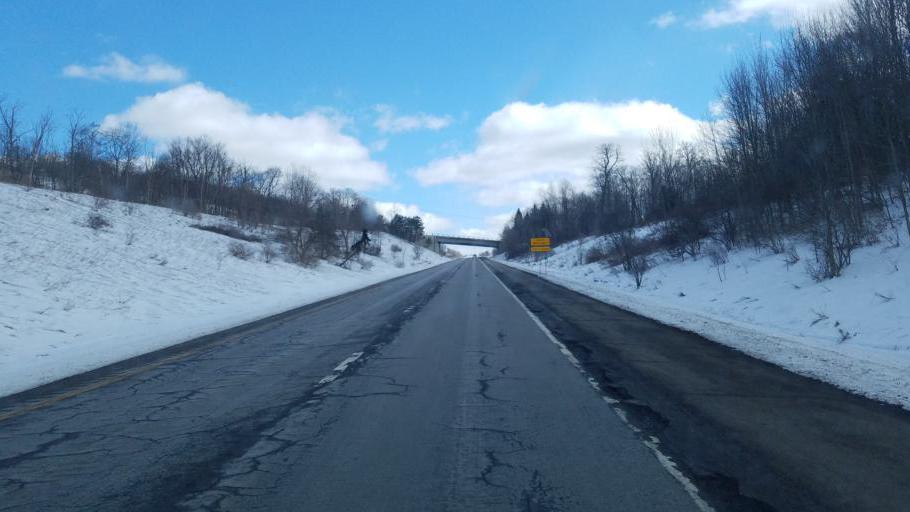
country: US
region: New York
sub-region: Chautauqua County
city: Lakewood
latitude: 42.1472
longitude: -79.3637
